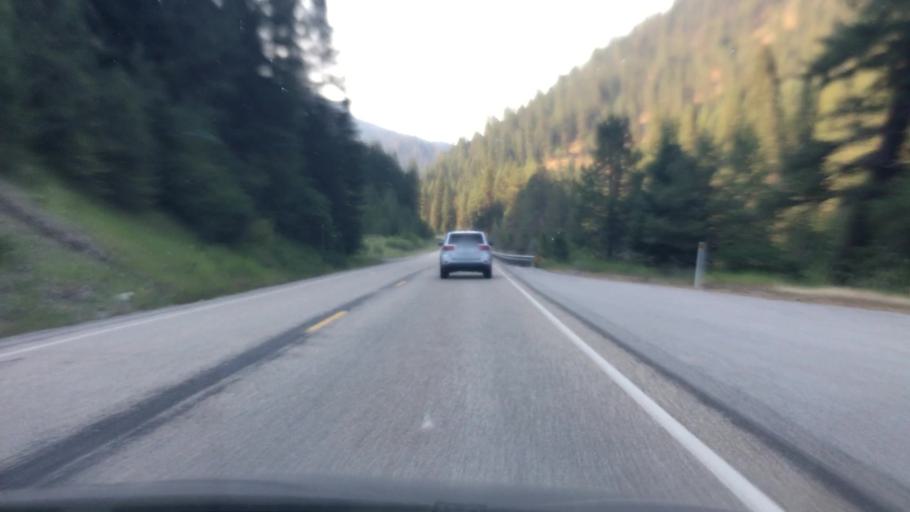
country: US
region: Idaho
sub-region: Valley County
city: Cascade
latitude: 44.1603
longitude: -116.1180
